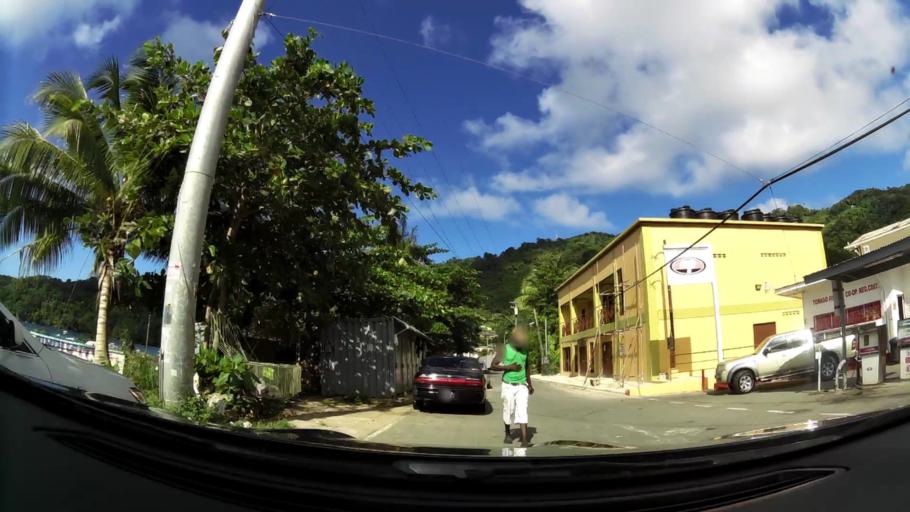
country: TT
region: Eastern Tobago
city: Roxborough
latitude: 11.3222
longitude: -60.5495
